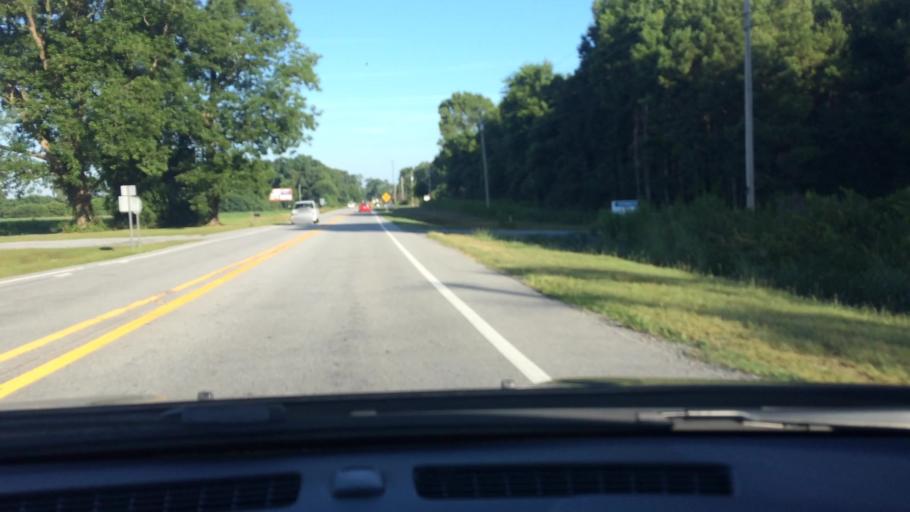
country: US
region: North Carolina
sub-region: Pitt County
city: Summerfield
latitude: 35.6299
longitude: -77.4359
